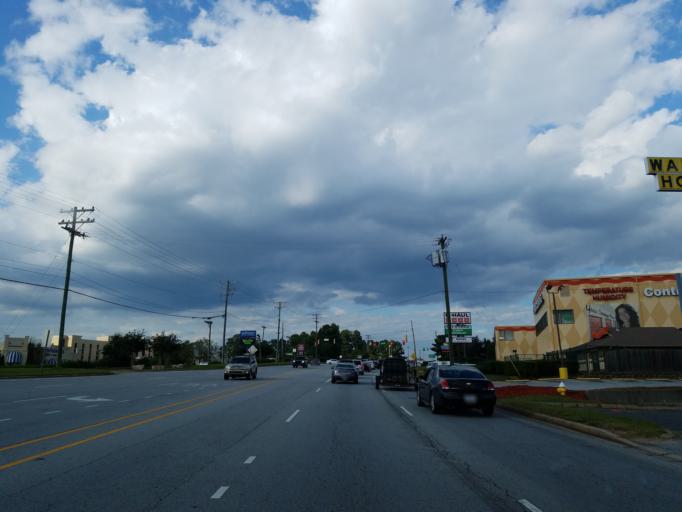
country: US
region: South Carolina
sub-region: Greenville County
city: Mauldin
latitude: 34.8370
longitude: -82.3159
